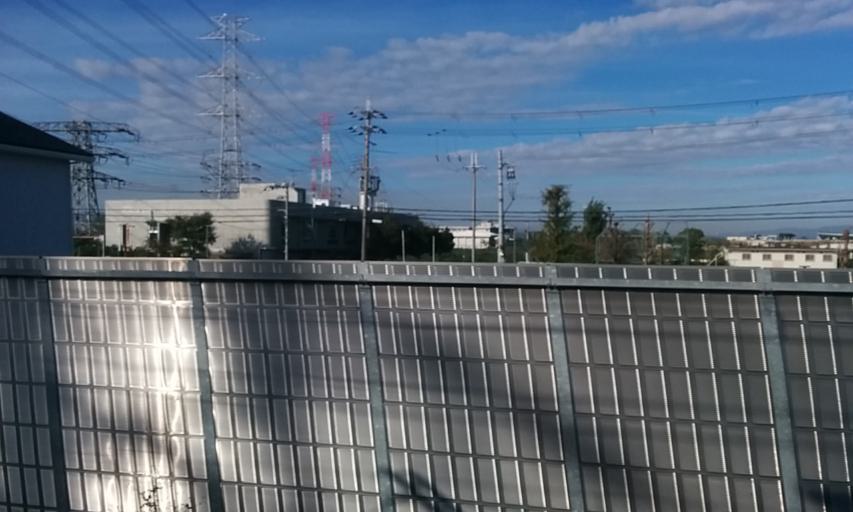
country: JP
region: Kyoto
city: Tanabe
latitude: 34.8441
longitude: 135.7724
